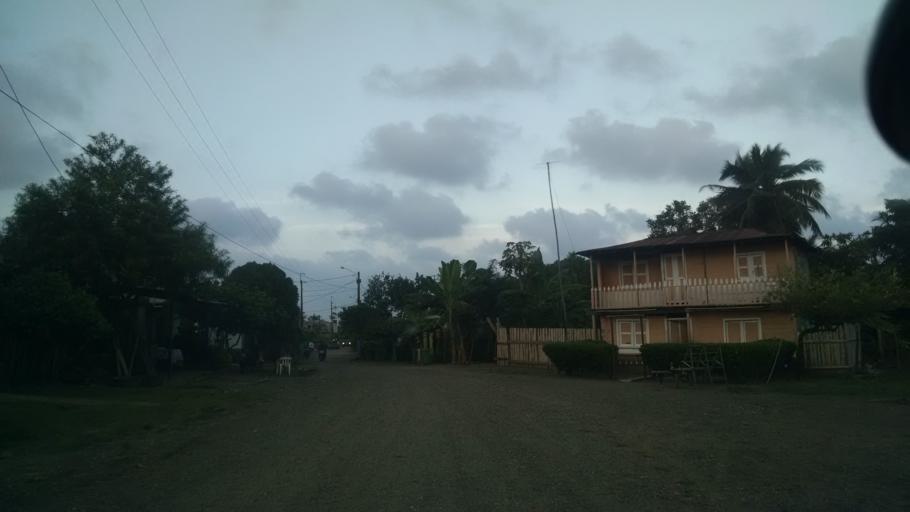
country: CO
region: Antioquia
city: San Juan de Uraba
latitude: 8.7365
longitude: -76.6072
